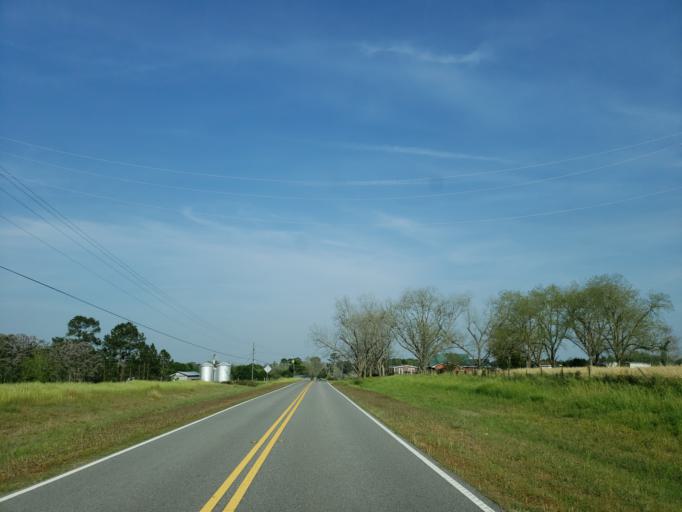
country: US
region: Georgia
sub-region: Tift County
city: Tifton
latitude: 31.5711
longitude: -83.5367
